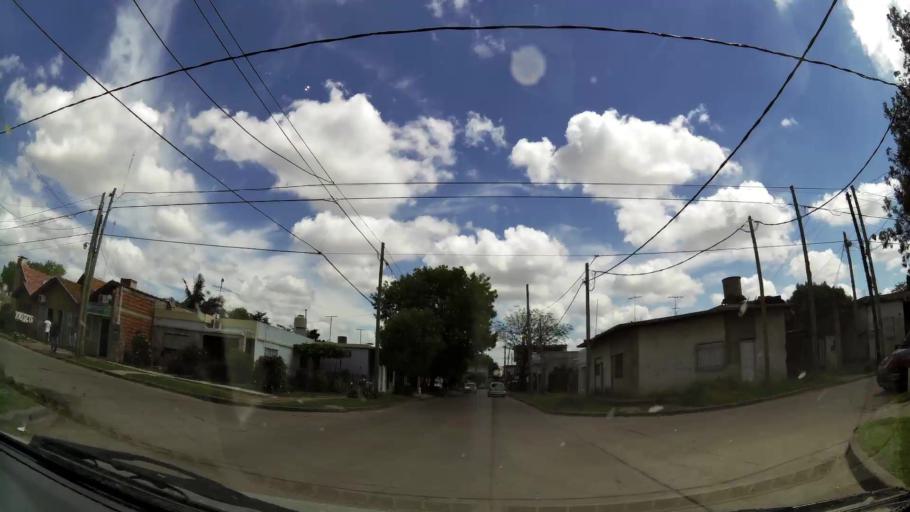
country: AR
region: Buenos Aires
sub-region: Partido de Quilmes
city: Quilmes
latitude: -34.8072
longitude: -58.2606
